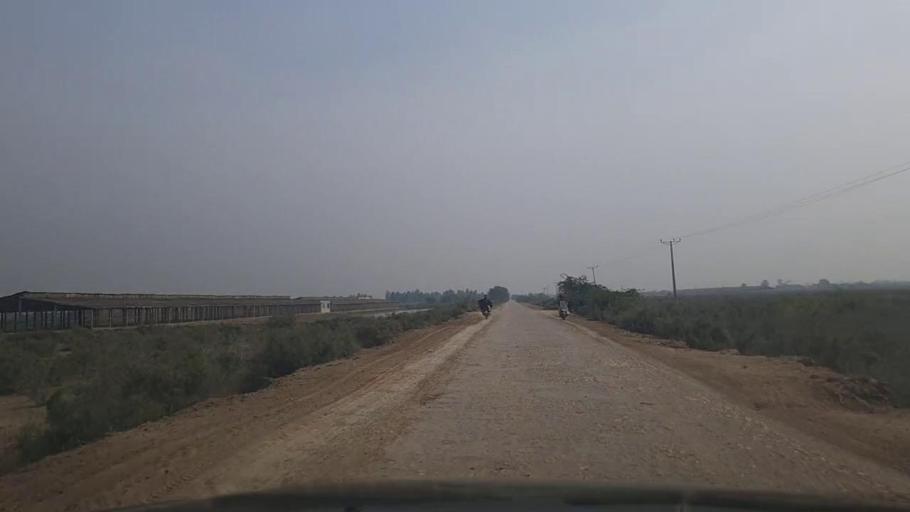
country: PK
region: Sindh
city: Mirpur Sakro
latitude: 24.4569
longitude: 67.7016
